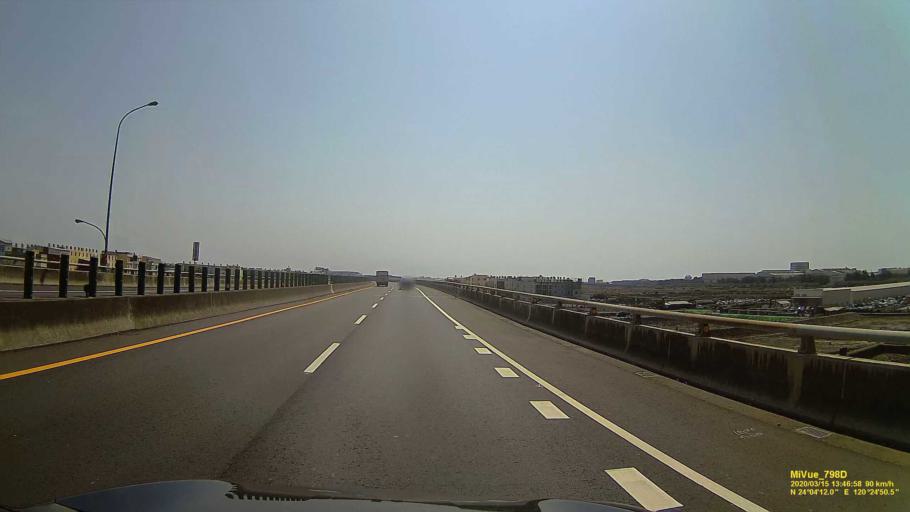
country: TW
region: Taiwan
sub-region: Changhua
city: Chang-hua
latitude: 24.0696
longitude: 120.4138
